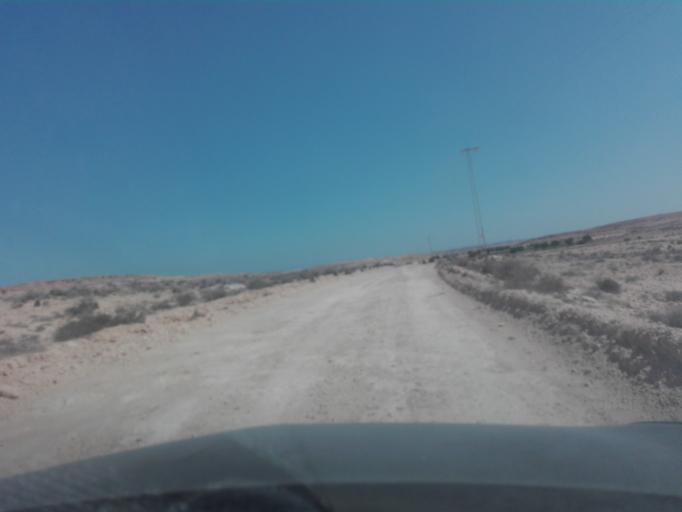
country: TN
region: Qabis
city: Gabes
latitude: 33.8441
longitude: 9.9826
